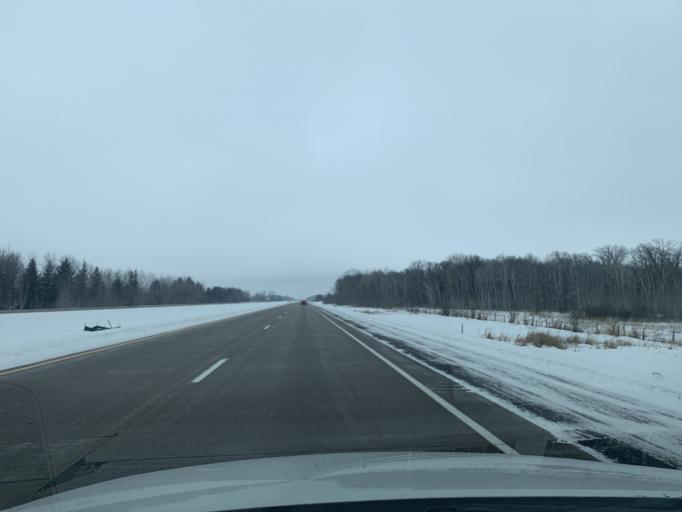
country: US
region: Minnesota
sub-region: Chisago County
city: Harris
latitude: 45.6355
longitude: -92.9921
